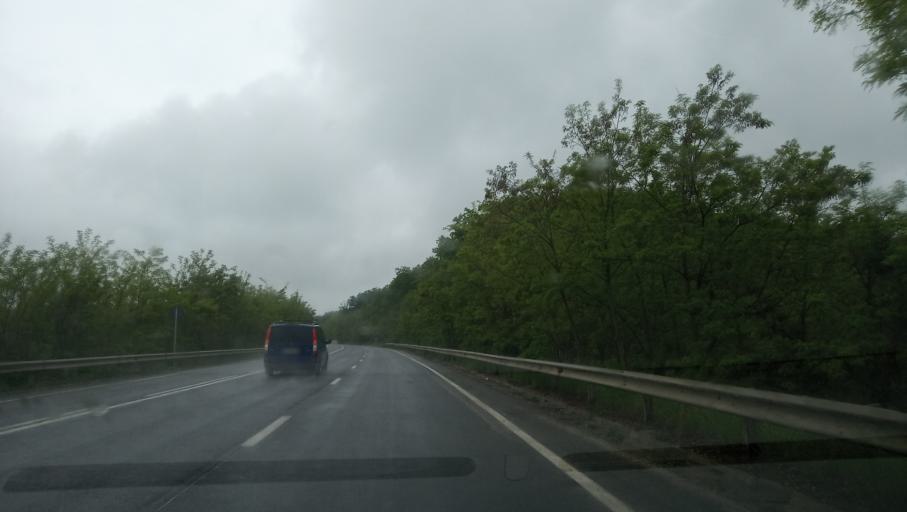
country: RO
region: Sibiu
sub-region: Comuna Orlat
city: Orlat
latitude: 45.7819
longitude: 23.9742
